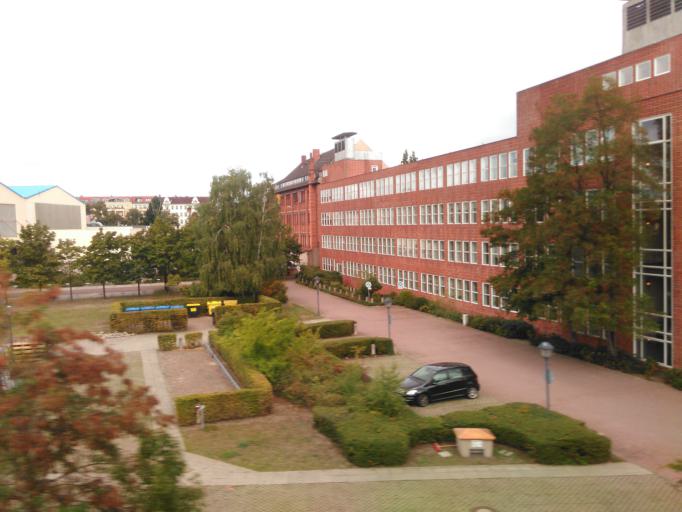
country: DE
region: Berlin
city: Wedding Bezirk
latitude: 52.5375
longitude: 13.3549
